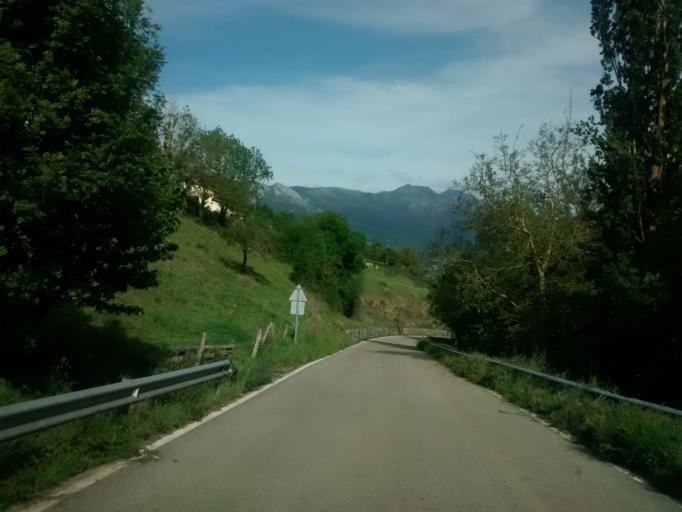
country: ES
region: Cantabria
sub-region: Provincia de Cantabria
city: Potes
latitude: 43.1926
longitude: -4.6381
